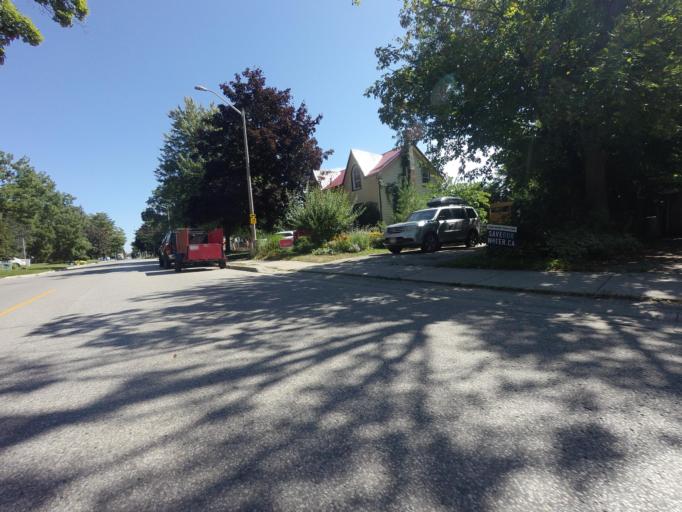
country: CA
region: Ontario
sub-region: Wellington County
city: Guelph
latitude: 43.7089
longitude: -80.3802
